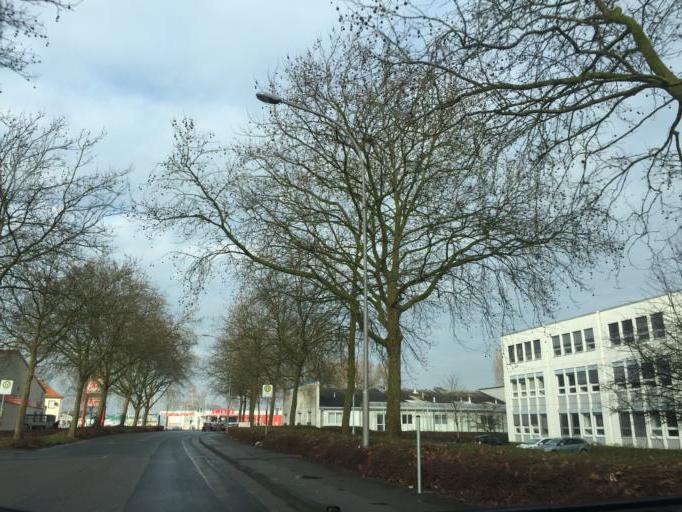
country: DE
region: North Rhine-Westphalia
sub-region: Regierungsbezirk Dusseldorf
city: Kleve
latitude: 51.7982
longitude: 6.1399
